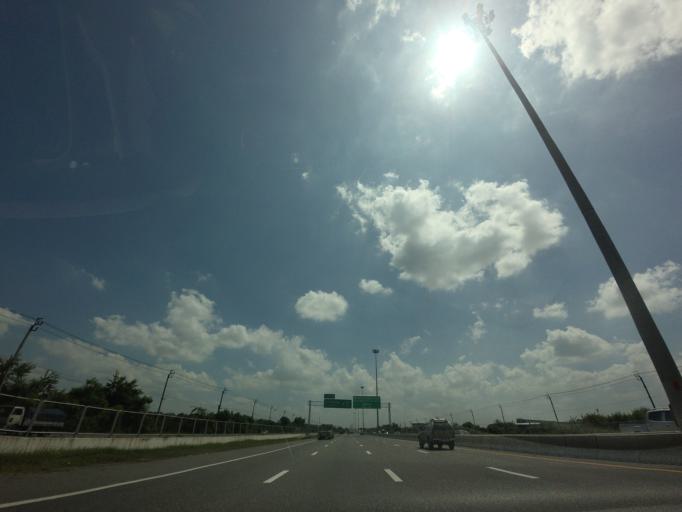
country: TH
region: Bangkok
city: Lat Krabang
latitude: 13.7212
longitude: 100.8148
